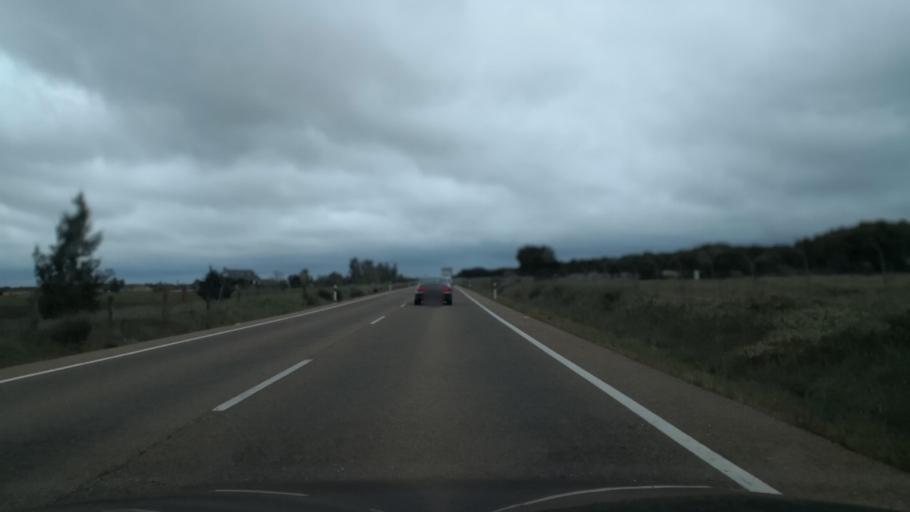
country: ES
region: Extremadura
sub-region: Provincia de Badajoz
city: Villar del Rey
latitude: 39.0095
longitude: -6.8573
